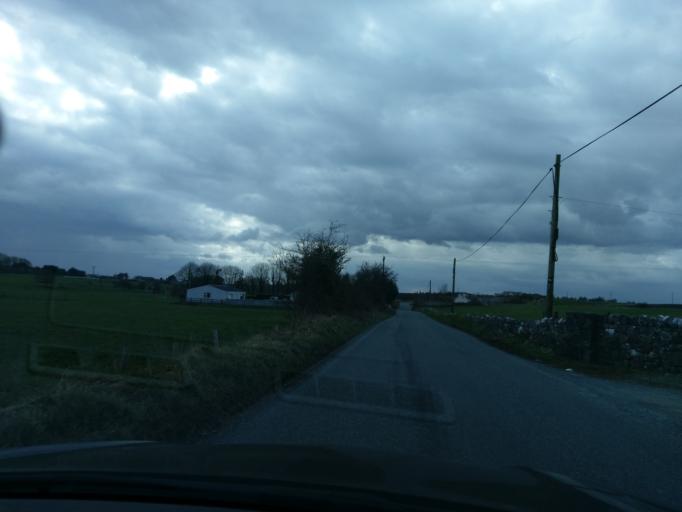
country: IE
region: Connaught
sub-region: County Galway
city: Athenry
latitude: 53.4723
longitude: -8.6537
